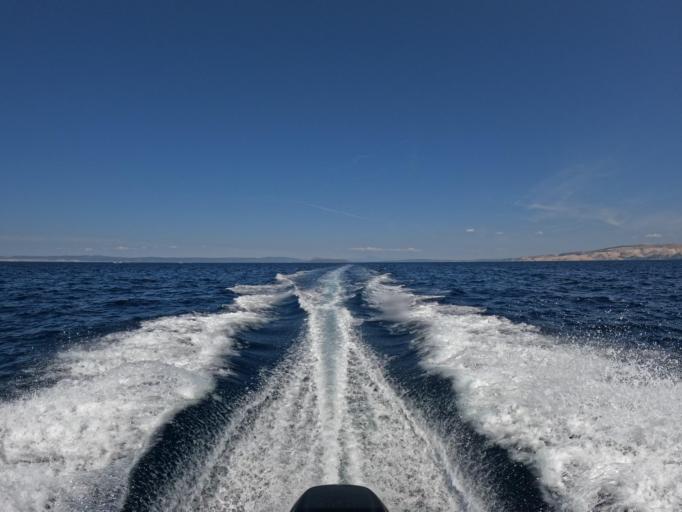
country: HR
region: Primorsko-Goranska
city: Lopar
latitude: 44.8818
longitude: 14.6562
